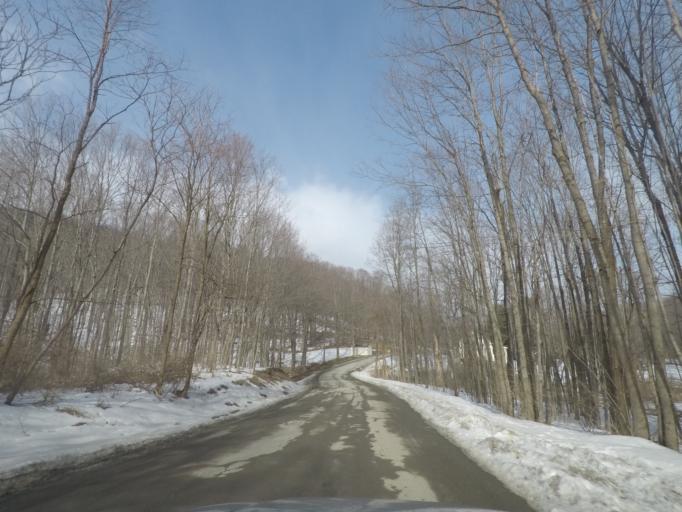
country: US
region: New York
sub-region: Saratoga County
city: Waterford
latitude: 42.7829
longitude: -73.5930
